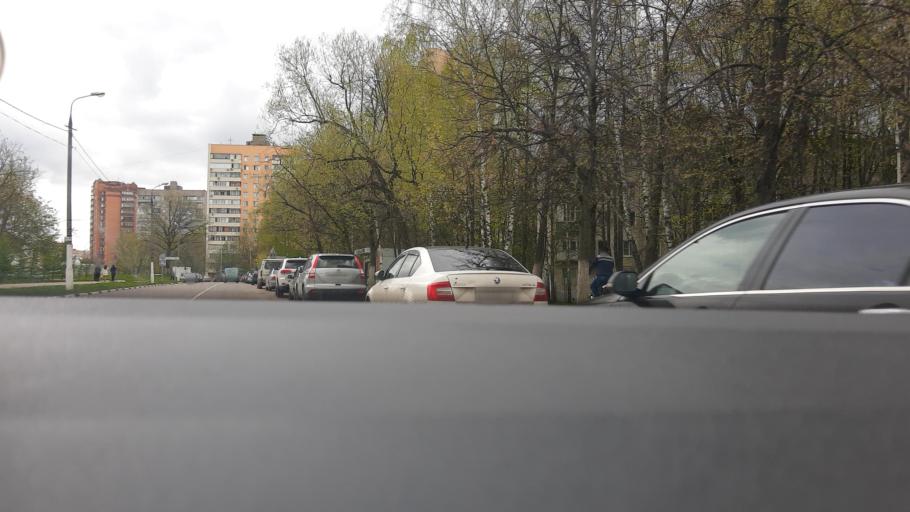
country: RU
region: Moskovskaya
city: Odintsovo
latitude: 55.6749
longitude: 37.2621
